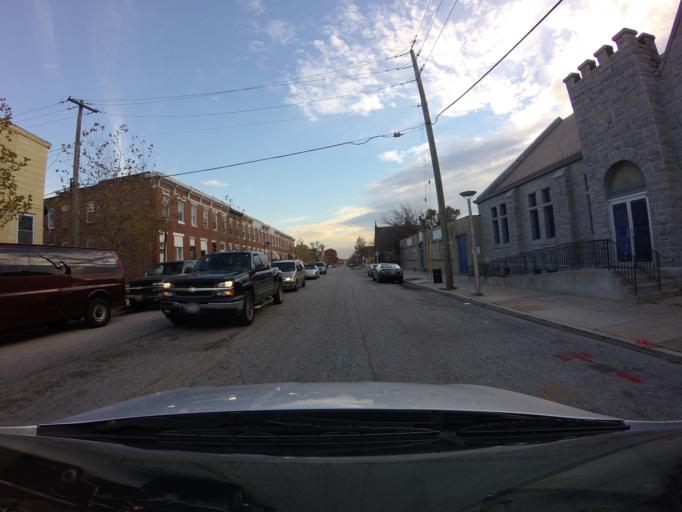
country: US
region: Maryland
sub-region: City of Baltimore
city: Baltimore
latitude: 39.2990
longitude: -76.5766
